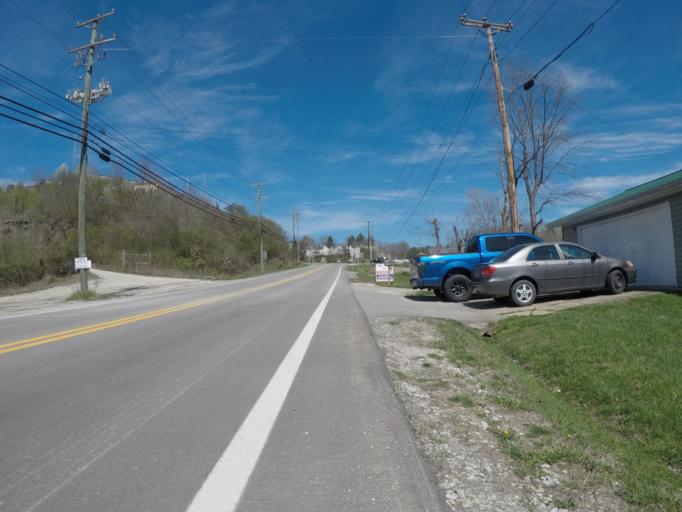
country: US
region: West Virginia
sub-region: Cabell County
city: Pea Ridge
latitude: 38.4098
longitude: -82.3203
